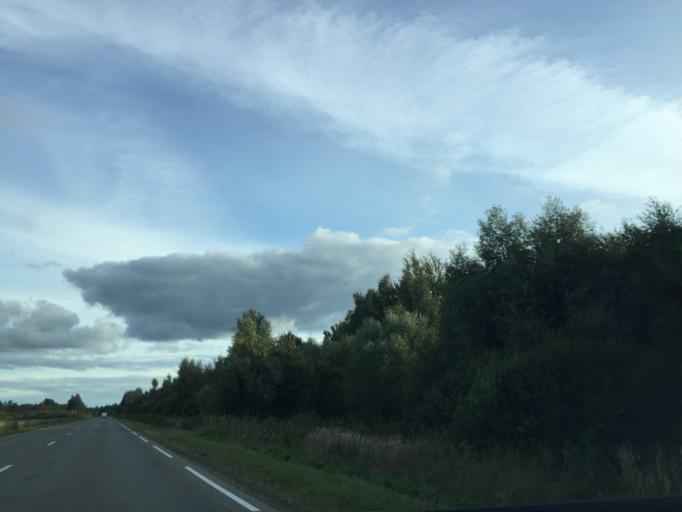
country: LV
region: Nereta
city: Nereta
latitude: 56.3187
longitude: 25.0930
